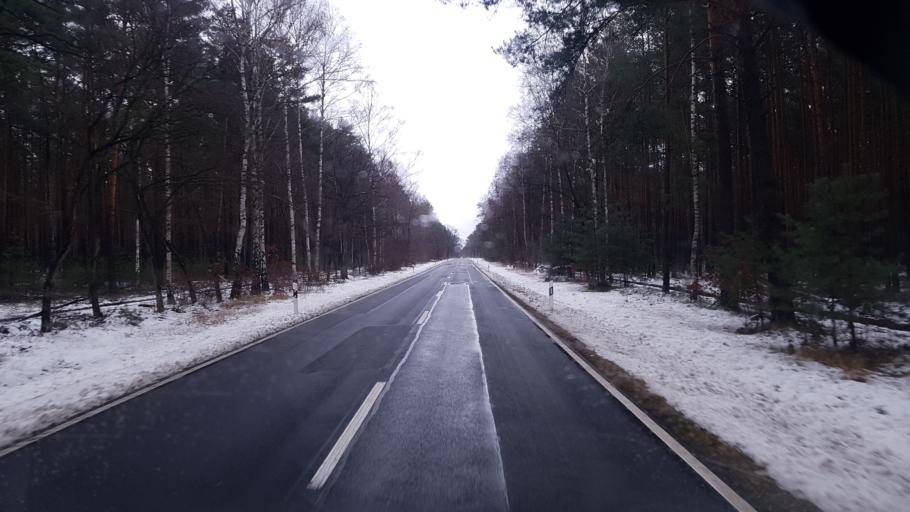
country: DE
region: Brandenburg
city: Tauer
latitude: 51.9796
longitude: 14.4888
